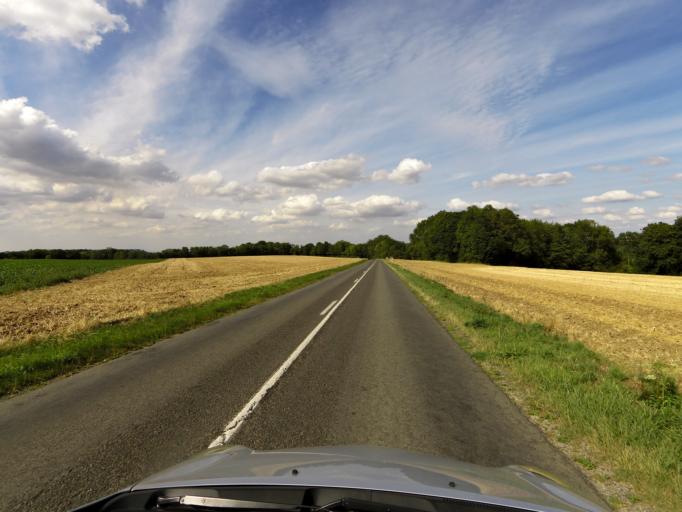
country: FR
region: Picardie
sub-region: Departement de l'Aisne
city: Bruyeres-et-Montberault
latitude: 49.5090
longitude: 3.6743
